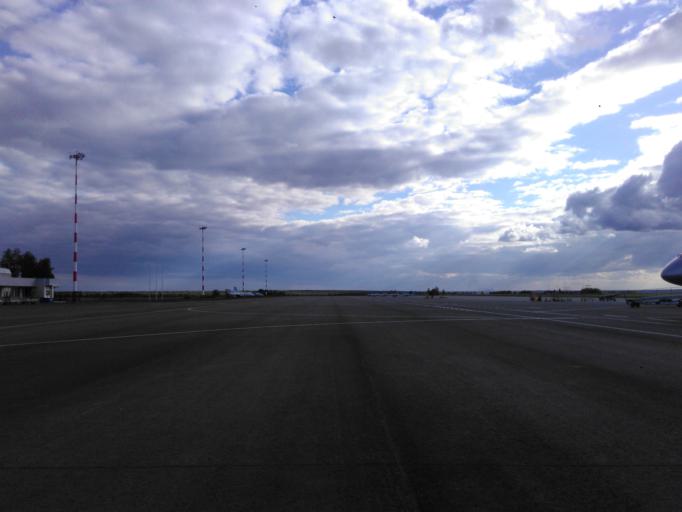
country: RU
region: Tatarstan
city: Yelabuga
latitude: 55.5653
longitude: 52.1013
